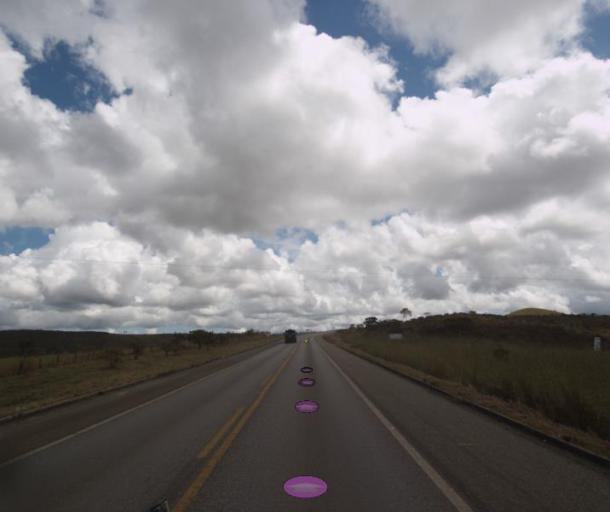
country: BR
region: Goias
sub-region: Pirenopolis
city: Pirenopolis
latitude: -15.7675
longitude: -48.7152
